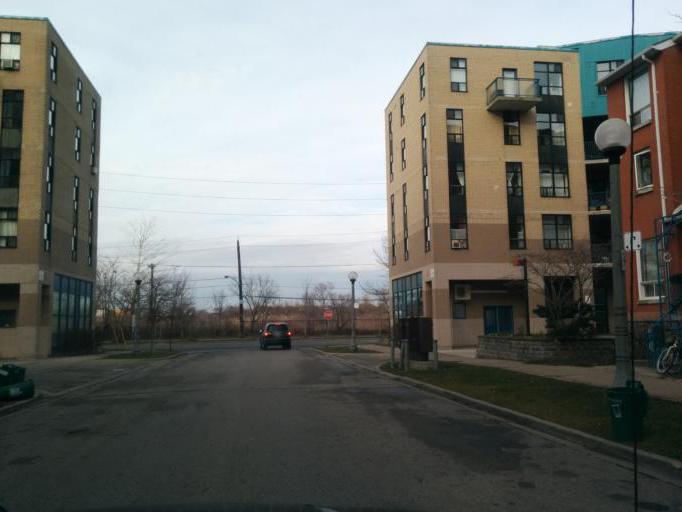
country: CA
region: Ontario
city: Etobicoke
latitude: 43.6018
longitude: -79.5098
